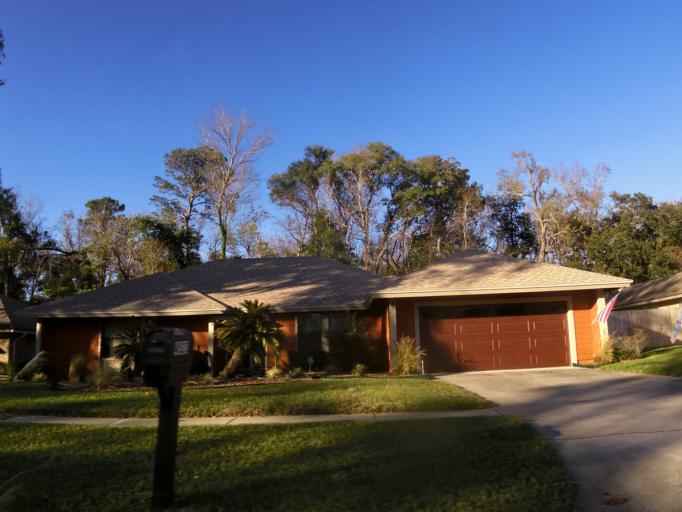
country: US
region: Florida
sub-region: Saint Johns County
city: Fruit Cove
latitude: 30.2141
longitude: -81.6039
